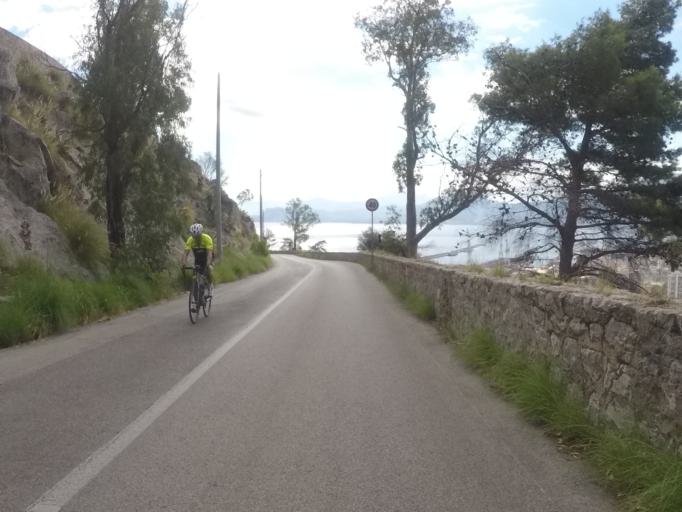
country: IT
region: Sicily
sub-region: Palermo
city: Palermo
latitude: 38.1522
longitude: 13.3615
